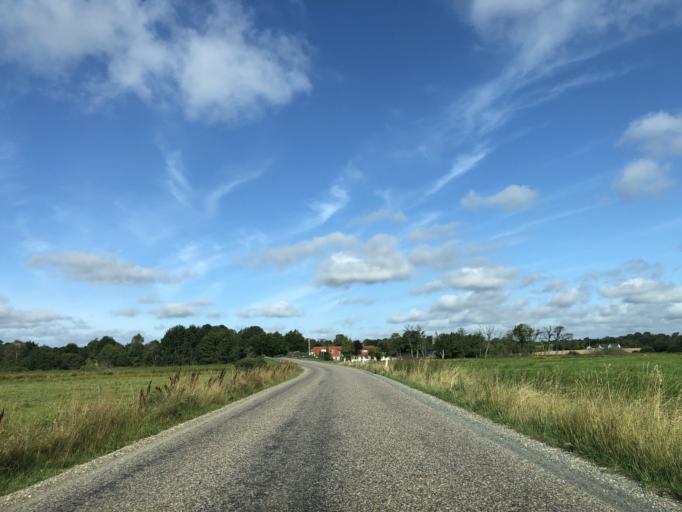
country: DK
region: Central Jutland
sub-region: Silkeborg Kommune
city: Svejbaek
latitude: 56.2221
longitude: 9.6721
